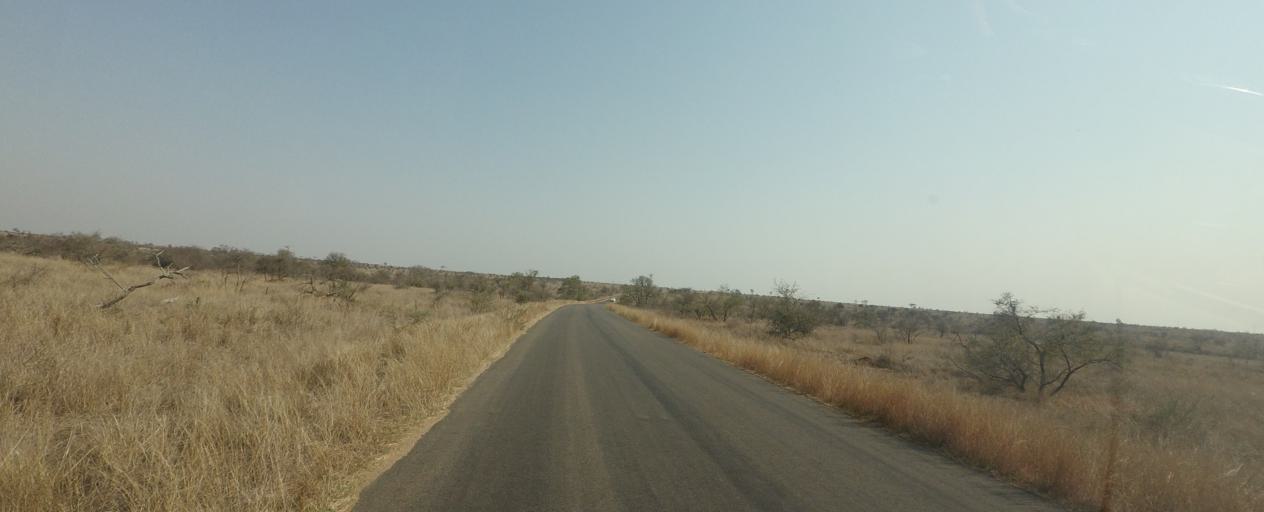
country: ZA
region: Limpopo
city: Thulamahashi
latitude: -24.3654
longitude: 31.7642
